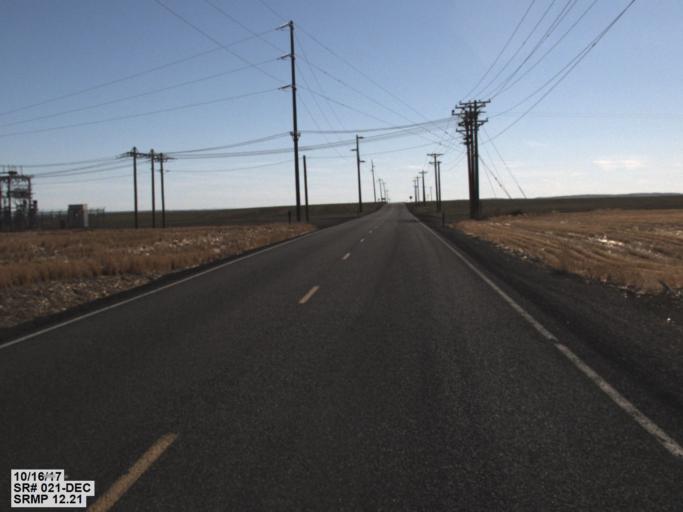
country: US
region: Washington
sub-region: Franklin County
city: Connell
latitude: 46.8031
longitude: -118.5473
